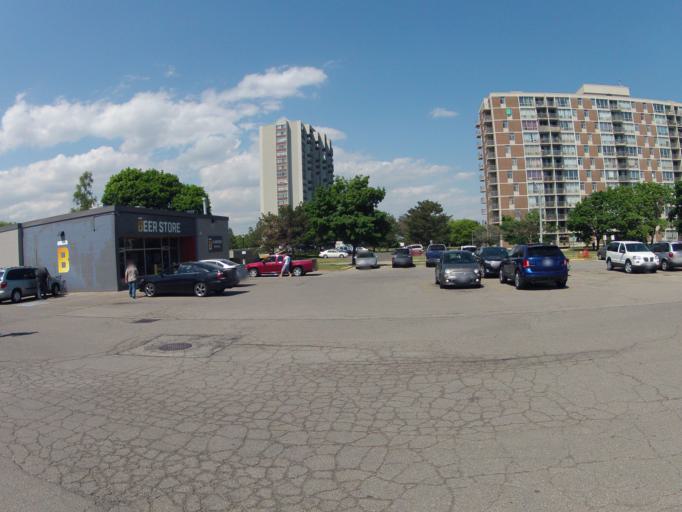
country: CA
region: Ontario
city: Mississauga
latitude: 43.5129
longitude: -79.6489
